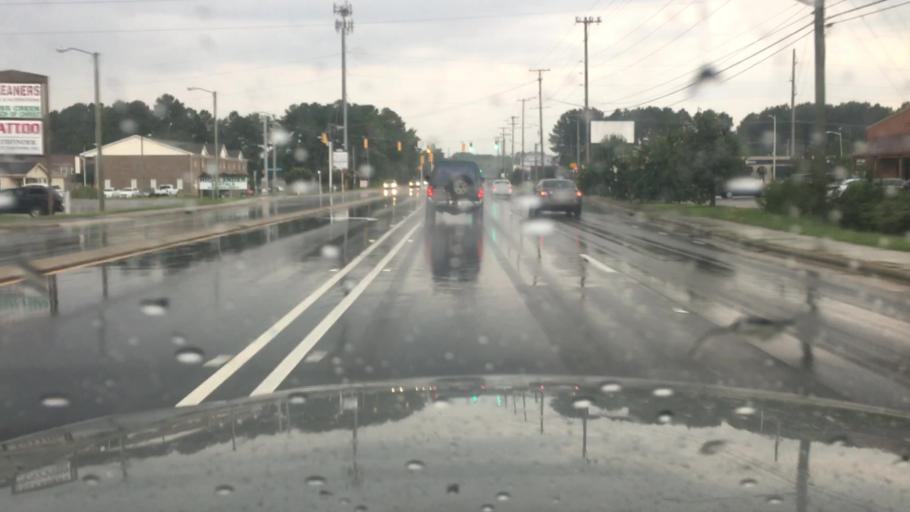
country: US
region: North Carolina
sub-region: Cumberland County
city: Fort Bragg
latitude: 35.0676
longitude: -79.0132
